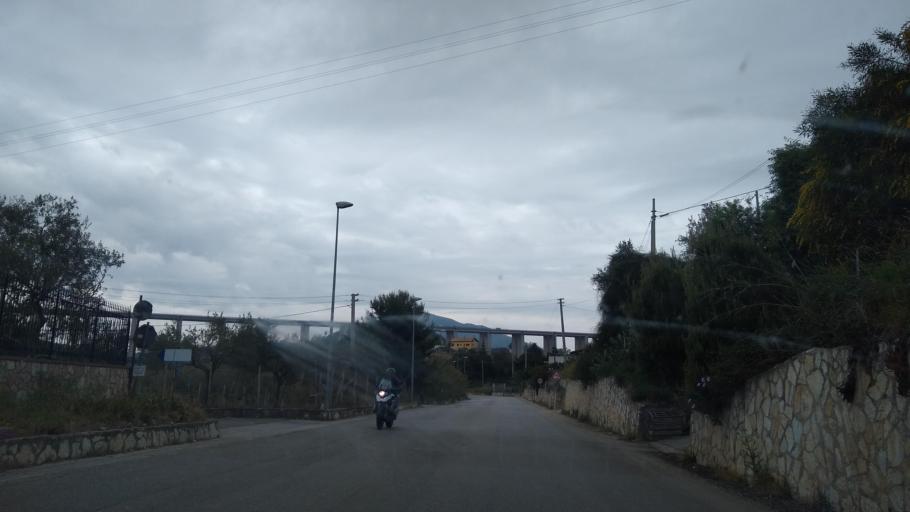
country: IT
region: Sicily
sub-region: Trapani
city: Alcamo
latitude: 38.0201
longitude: 12.9502
